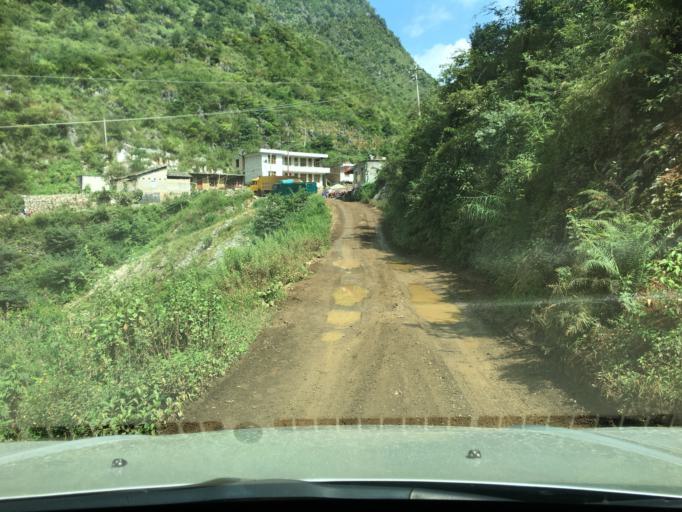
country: CN
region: Guizhou Sheng
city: Liupanshui
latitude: 25.9098
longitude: 105.0997
